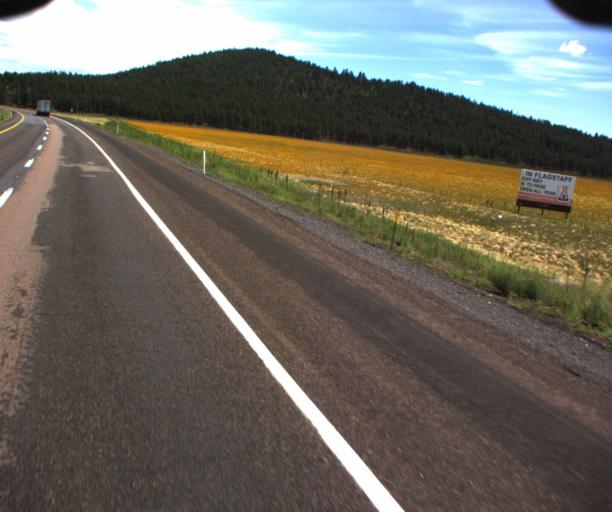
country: US
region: Arizona
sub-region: Coconino County
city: Williams
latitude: 35.2580
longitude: -112.0807
